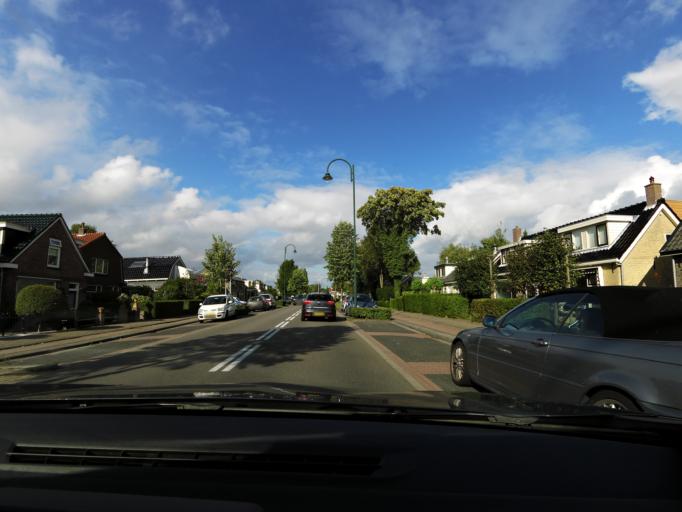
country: NL
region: South Holland
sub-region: Gemeente Hellevoetsluis
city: Nieuw-Helvoet
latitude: 51.8409
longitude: 4.1361
